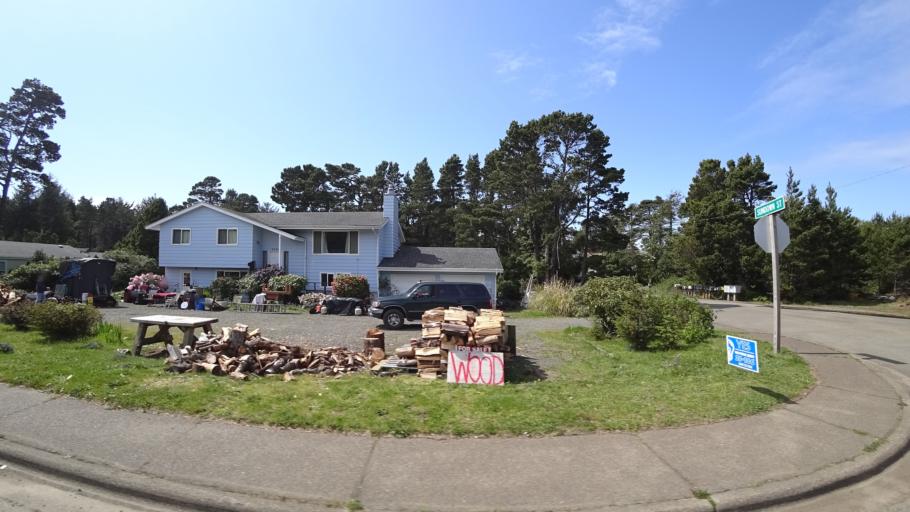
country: US
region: Oregon
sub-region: Lincoln County
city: Lincoln Beach
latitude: 44.8462
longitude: -124.0464
